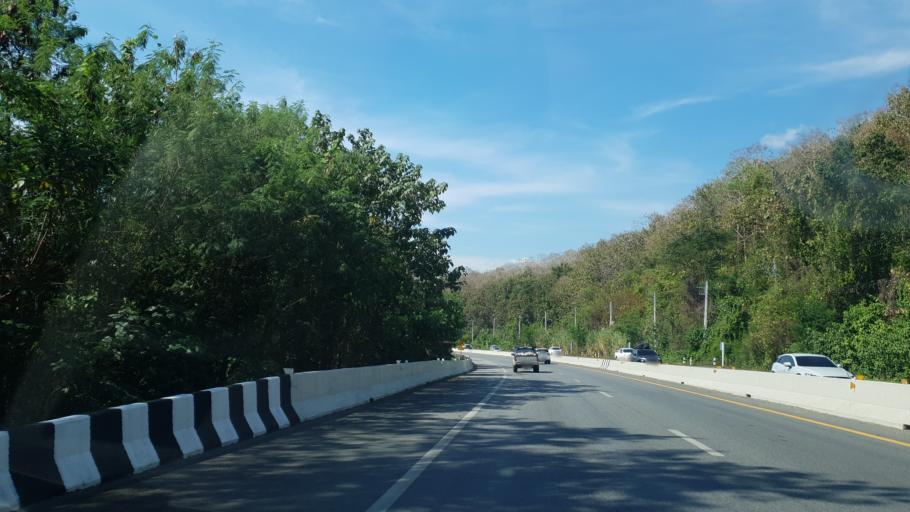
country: TH
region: Uttaradit
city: Lap Lae
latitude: 17.7794
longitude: 100.1221
